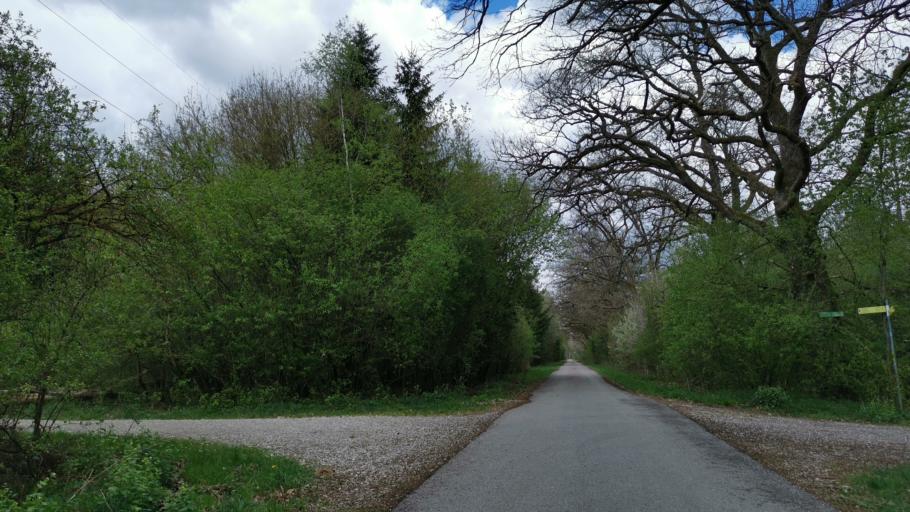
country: DE
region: Bavaria
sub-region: Upper Bavaria
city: Neuried
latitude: 48.0559
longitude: 11.4561
